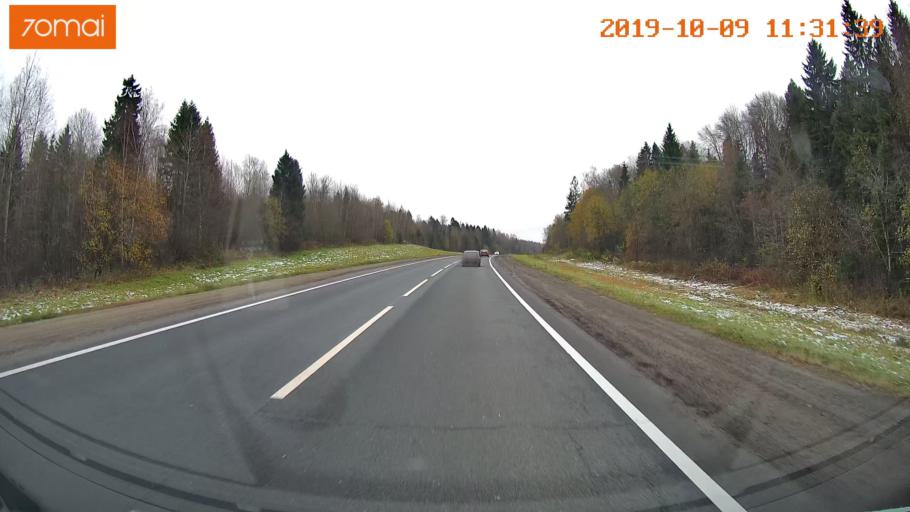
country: RU
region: Vologda
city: Gryazovets
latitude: 59.0435
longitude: 40.1001
